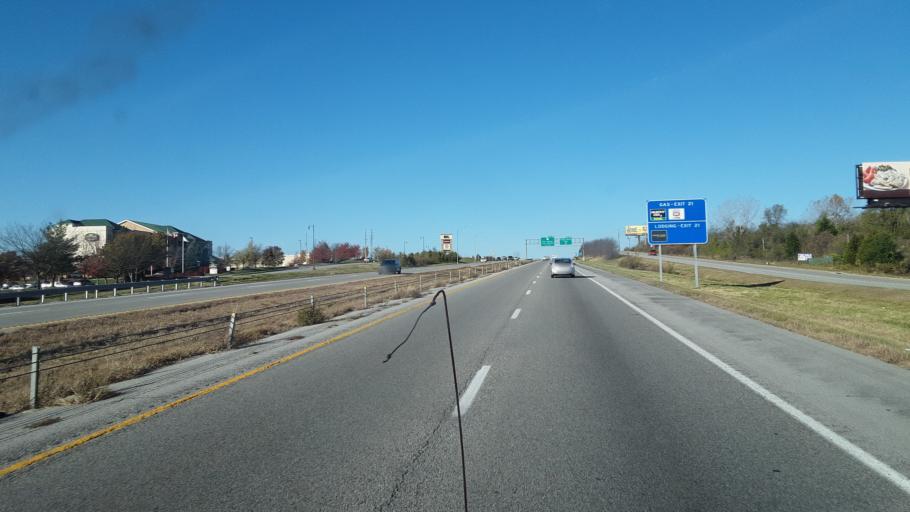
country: US
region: Missouri
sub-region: Jackson County
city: Grain Valley
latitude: 39.0269
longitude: -94.2396
